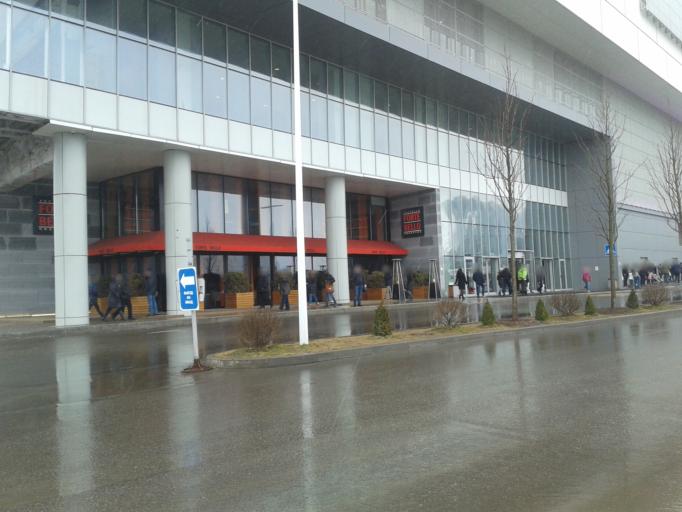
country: RU
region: Moscow
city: Strogino
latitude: 55.8218
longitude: 37.3853
